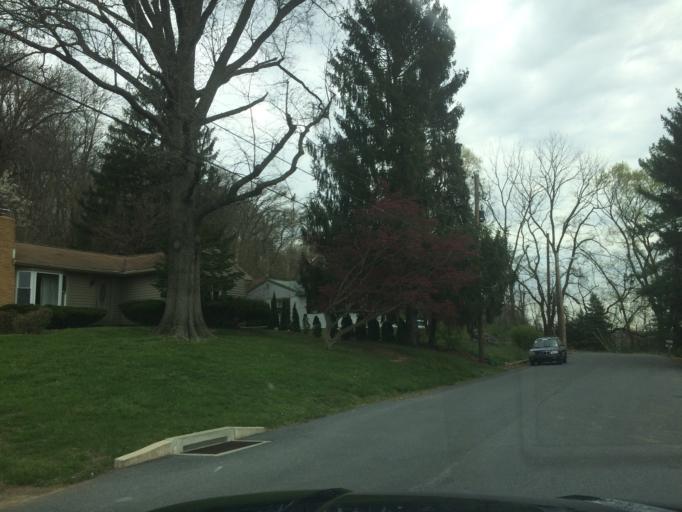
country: US
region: Pennsylvania
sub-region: Lancaster County
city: East Petersburg
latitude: 40.0557
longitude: -76.3728
